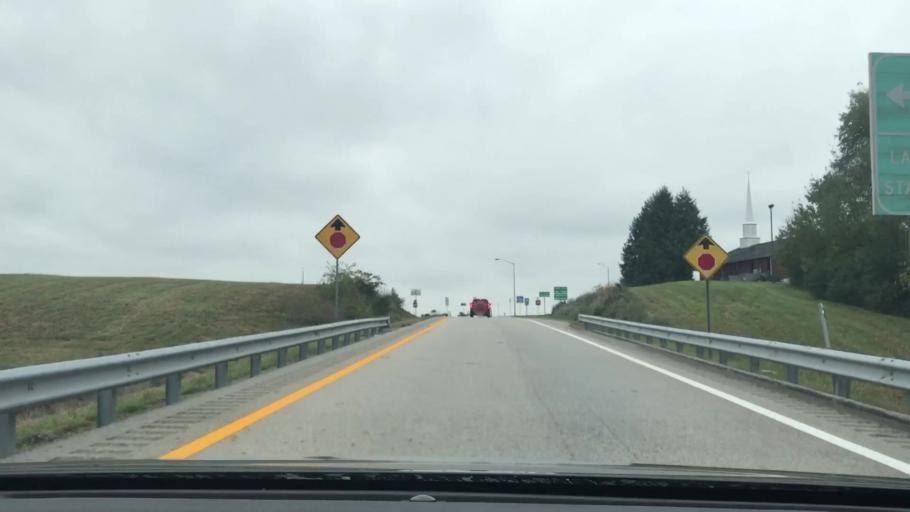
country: US
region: Kentucky
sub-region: Adair County
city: Columbia
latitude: 37.0871
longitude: -85.3042
